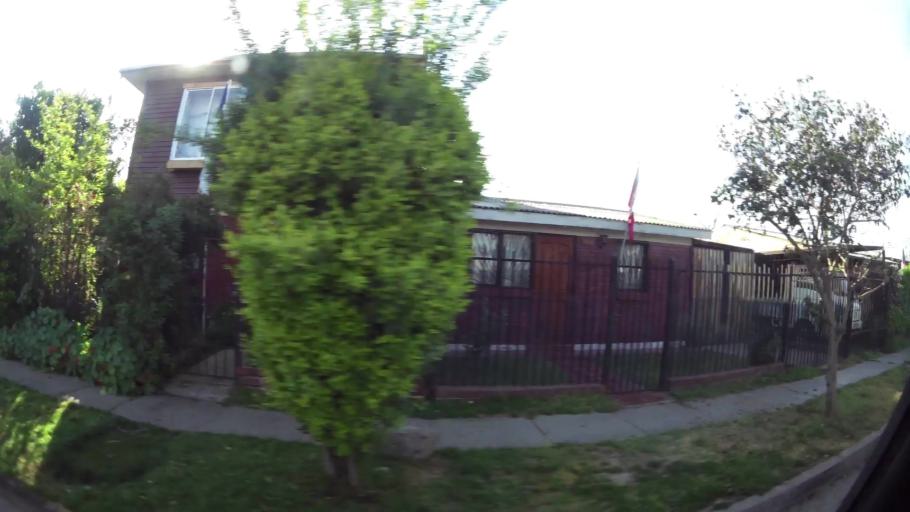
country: CL
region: Santiago Metropolitan
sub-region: Provincia de Santiago
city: Lo Prado
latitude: -33.4388
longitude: -70.7473
